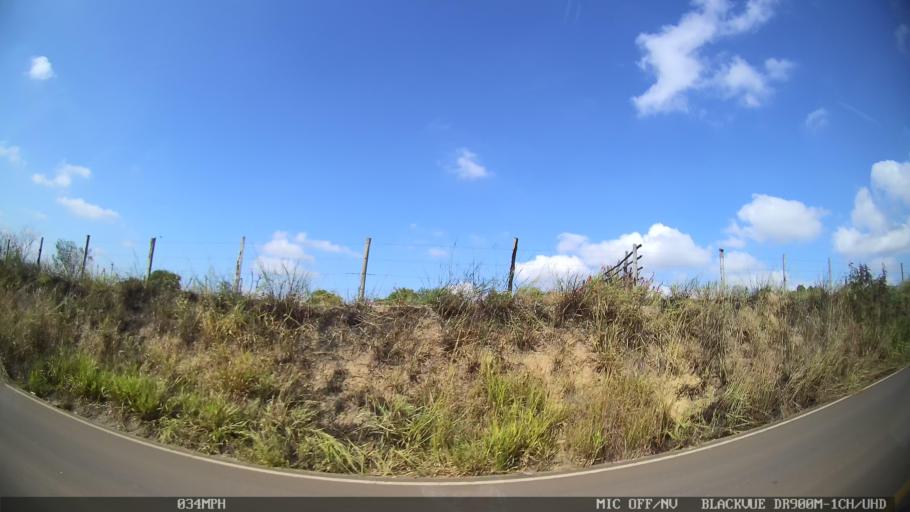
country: BR
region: Sao Paulo
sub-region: Indaiatuba
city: Indaiatuba
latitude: -22.9943
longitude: -47.1931
